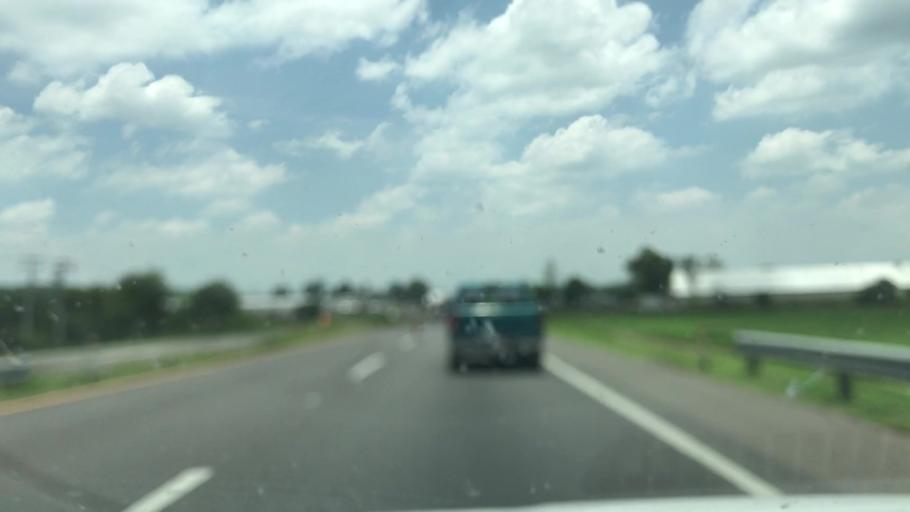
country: MX
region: Guanajuato
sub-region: Irapuato
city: San Ignacio de Rivera (Ojo de Agua)
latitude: 20.5280
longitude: -101.4612
